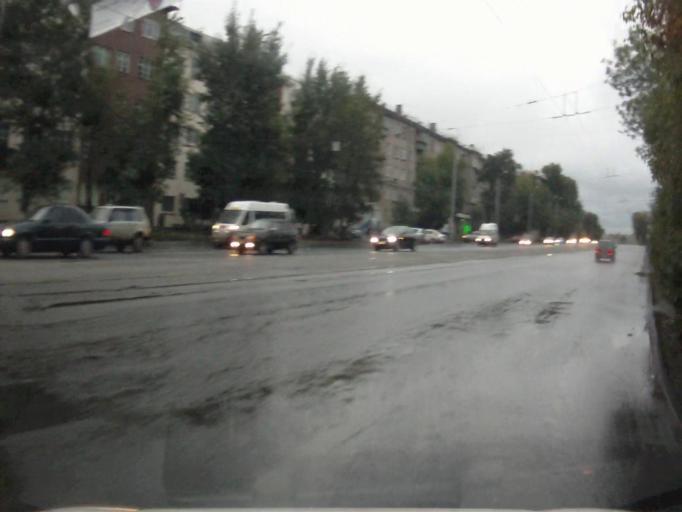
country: RU
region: Chelyabinsk
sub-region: Gorod Chelyabinsk
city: Chelyabinsk
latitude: 55.1598
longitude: 61.4450
